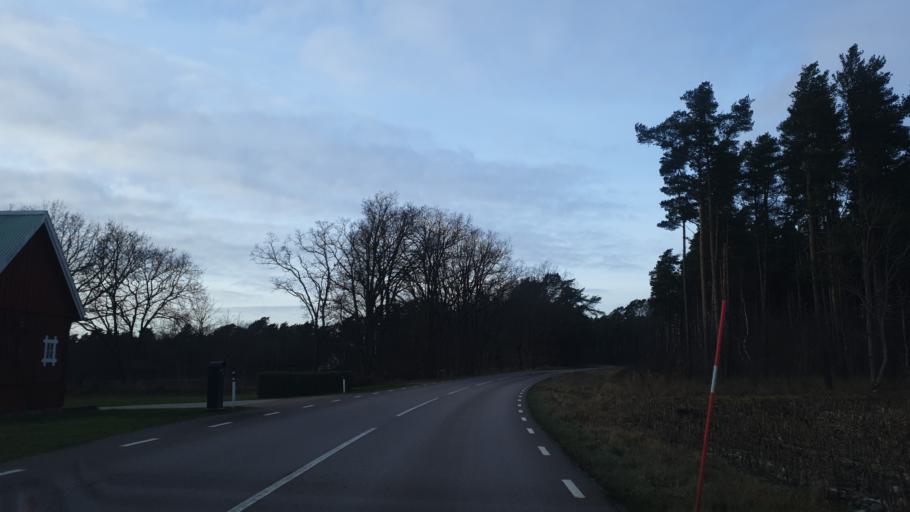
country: SE
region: Kalmar
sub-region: Torsas Kommun
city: Torsas
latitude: 56.2531
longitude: 16.0186
